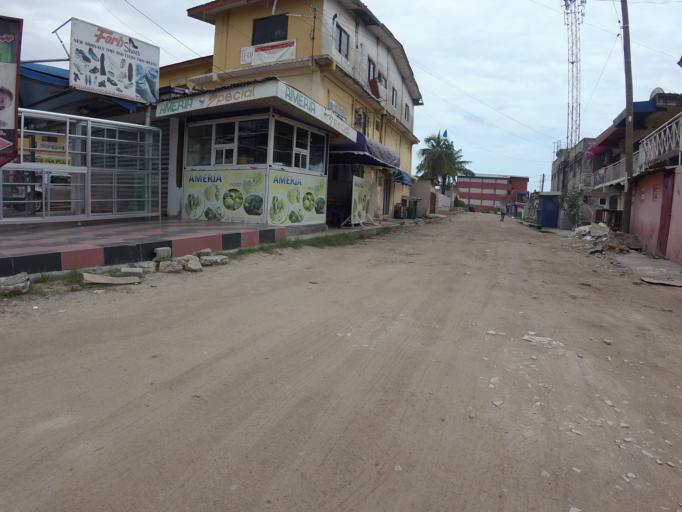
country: GH
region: Greater Accra
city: Dome
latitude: 5.6079
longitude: -0.2070
